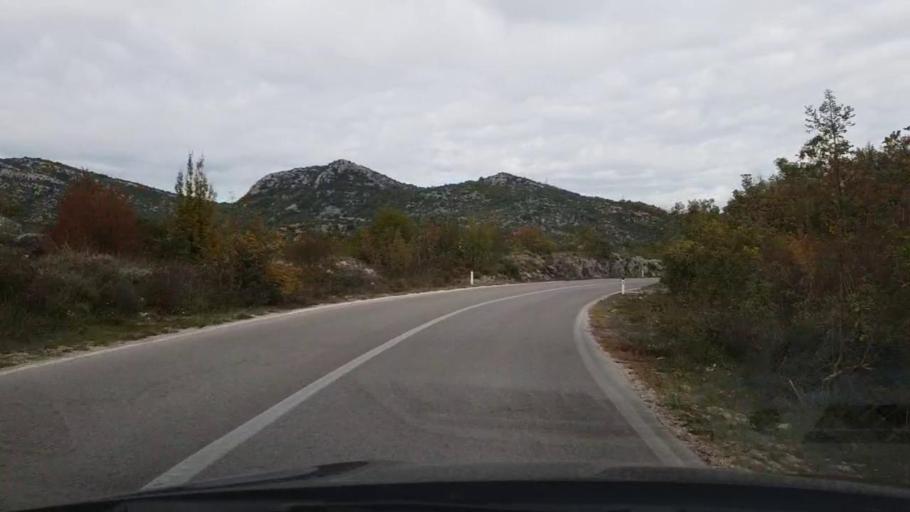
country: HR
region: Dubrovacko-Neretvanska
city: Cibaca
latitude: 42.6659
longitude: 18.2164
